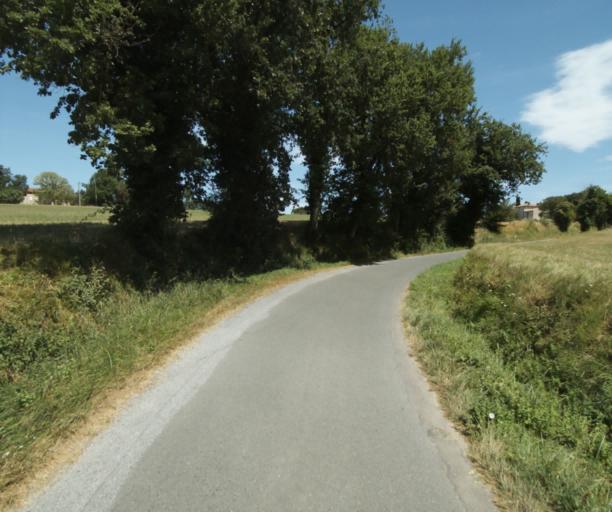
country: FR
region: Midi-Pyrenees
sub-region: Departement du Tarn
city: Soreze
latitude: 43.4900
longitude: 2.0529
